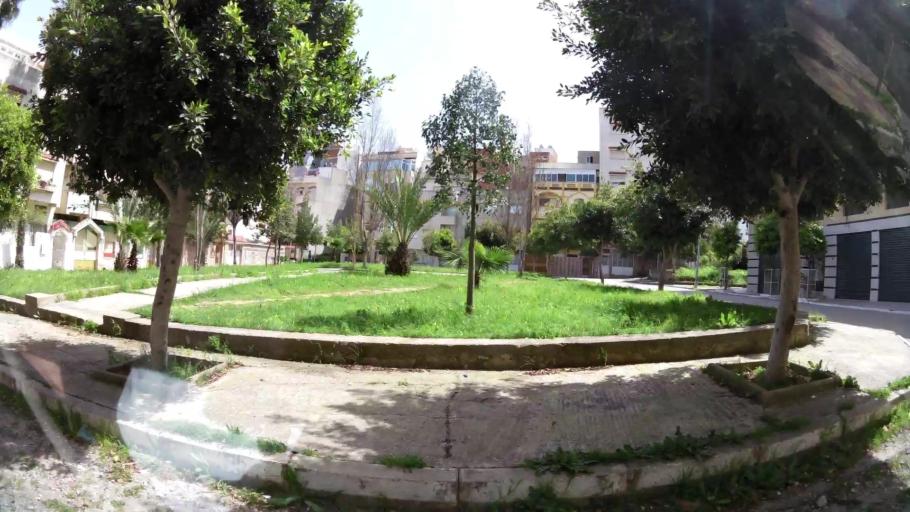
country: MA
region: Tanger-Tetouan
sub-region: Tanger-Assilah
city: Tangier
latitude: 35.7558
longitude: -5.8369
